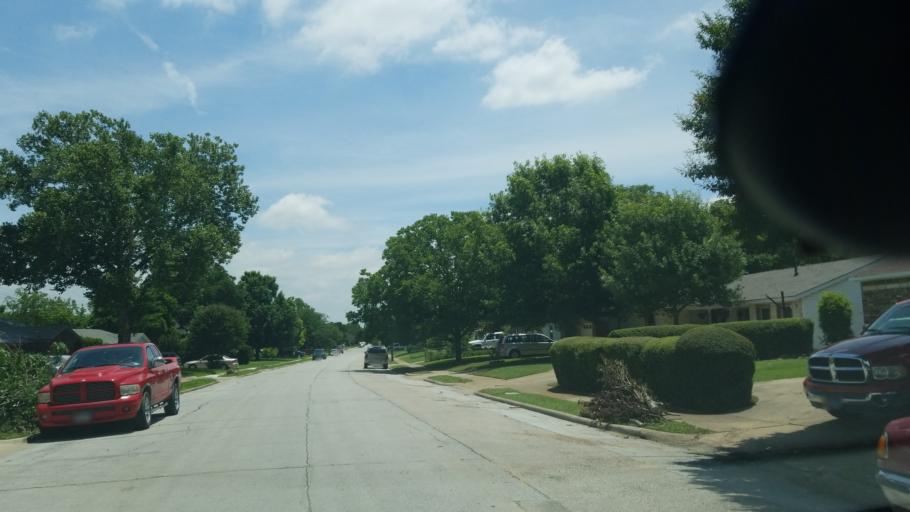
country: US
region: Texas
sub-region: Dallas County
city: Irving
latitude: 32.8512
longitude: -96.9708
